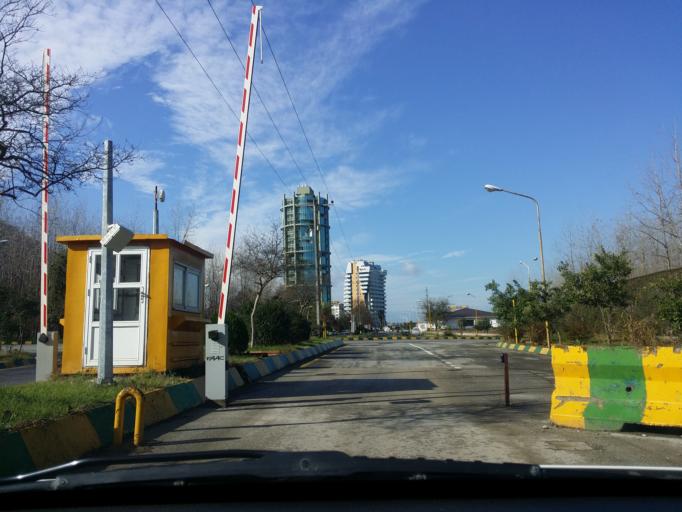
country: IR
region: Mazandaran
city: Chalus
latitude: 36.6676
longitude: 51.3078
